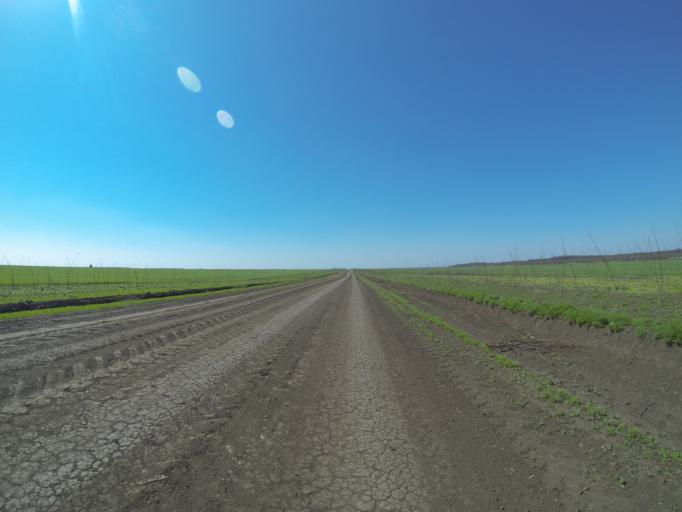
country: RO
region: Dolj
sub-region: Comuna Caloparu
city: Salcuta
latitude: 44.1377
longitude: 23.7295
